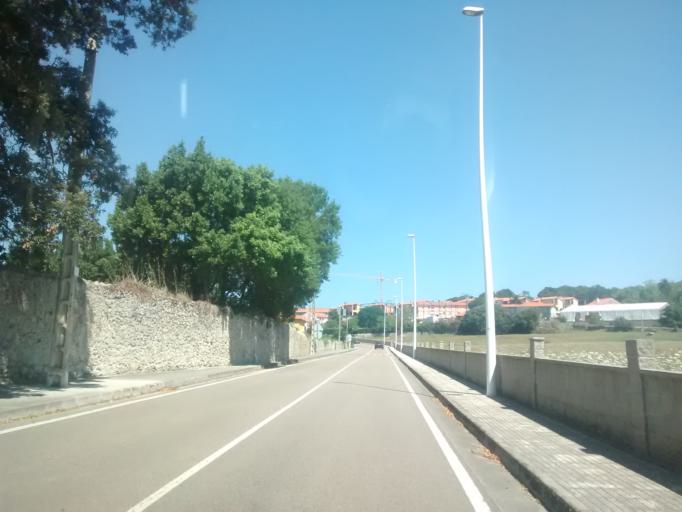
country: ES
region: Cantabria
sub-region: Provincia de Cantabria
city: Arnuero
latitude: 43.4741
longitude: -3.5693
